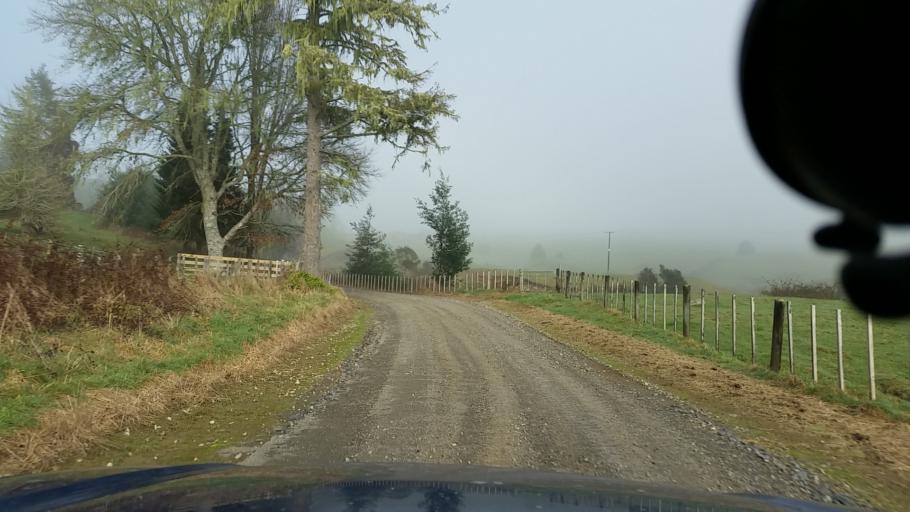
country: NZ
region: Taranaki
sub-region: New Plymouth District
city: Waitara
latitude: -38.9941
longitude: 174.7747
